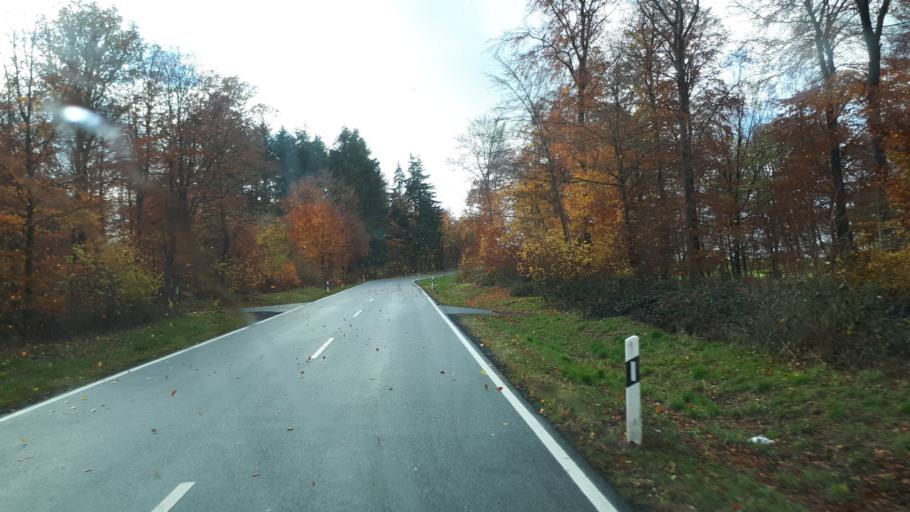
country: DE
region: Rheinland-Pfalz
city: Leienkaul
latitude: 50.1929
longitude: 7.0797
